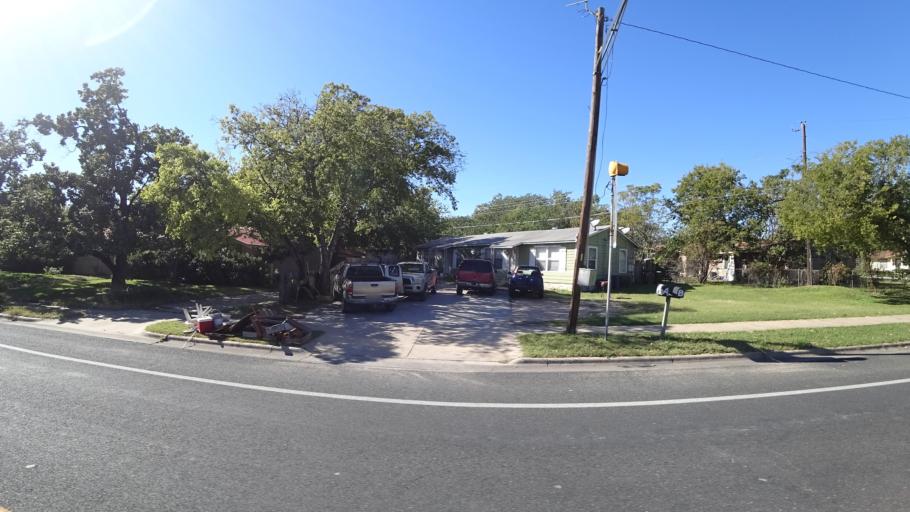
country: US
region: Texas
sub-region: Travis County
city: Austin
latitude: 30.2820
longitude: -97.6851
